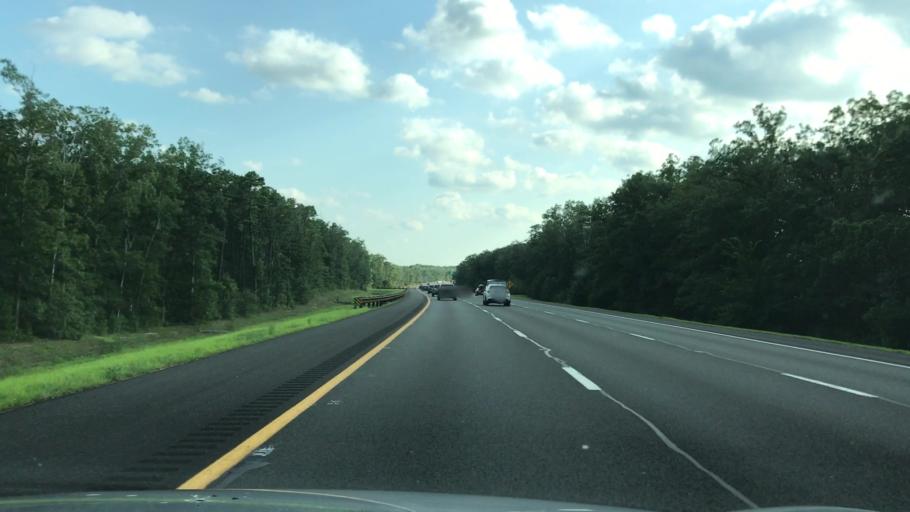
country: US
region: New Jersey
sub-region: Ocean County
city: Ocean Acres
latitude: 39.7184
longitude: -74.2751
